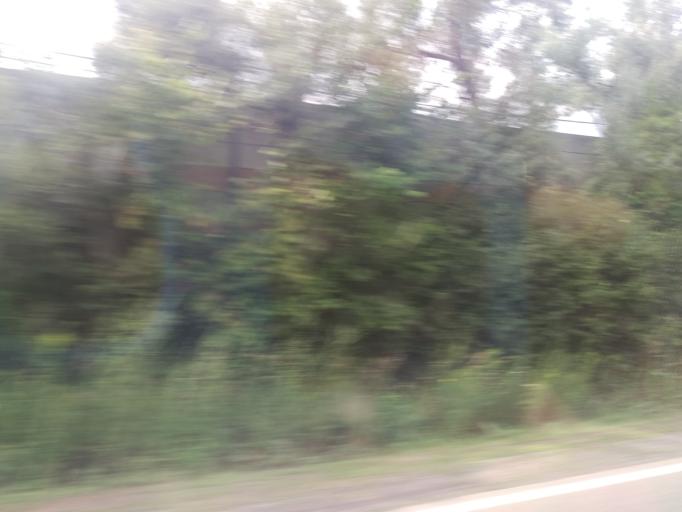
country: CA
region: Ontario
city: Mississauga
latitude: 43.5285
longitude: -79.6426
